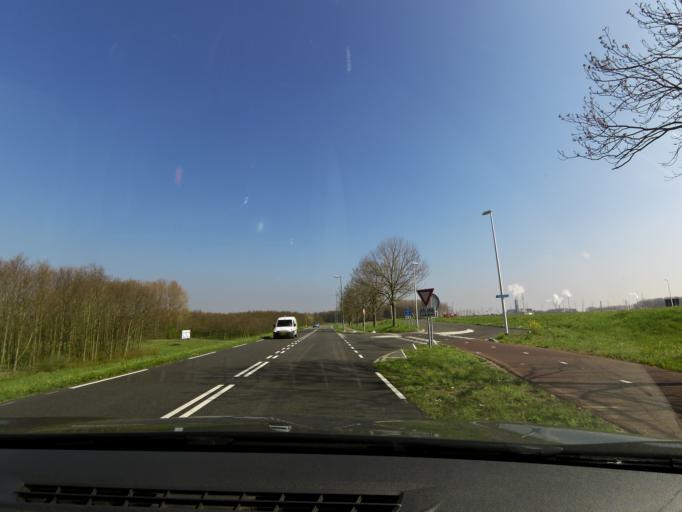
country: NL
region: South Holland
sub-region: Gemeente Maassluis
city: Maassluis
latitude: 51.9106
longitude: 4.2665
